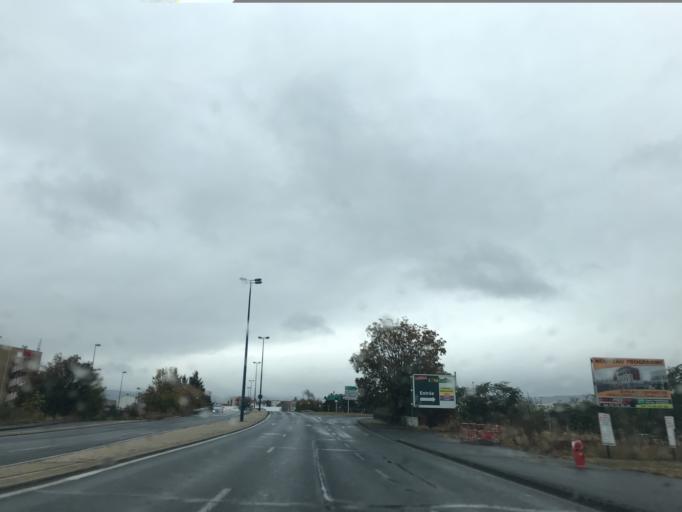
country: FR
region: Auvergne
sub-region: Departement du Puy-de-Dome
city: Aubiere
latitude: 45.7796
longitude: 3.1201
